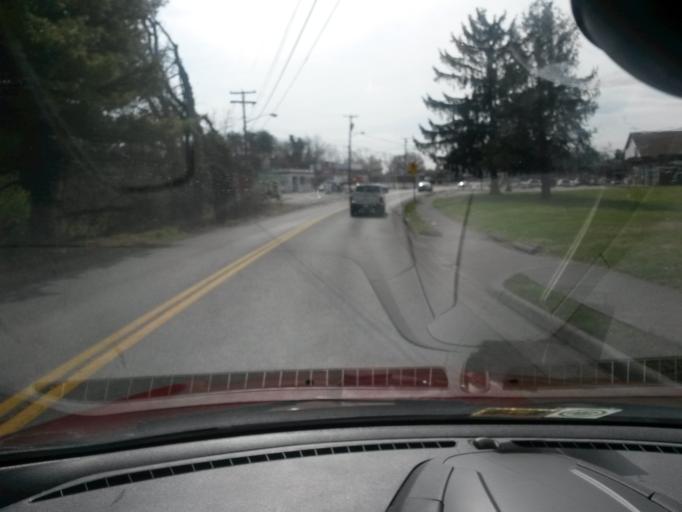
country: US
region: Virginia
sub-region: City of Roanoke
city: Roanoke
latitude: 37.2986
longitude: -79.9733
